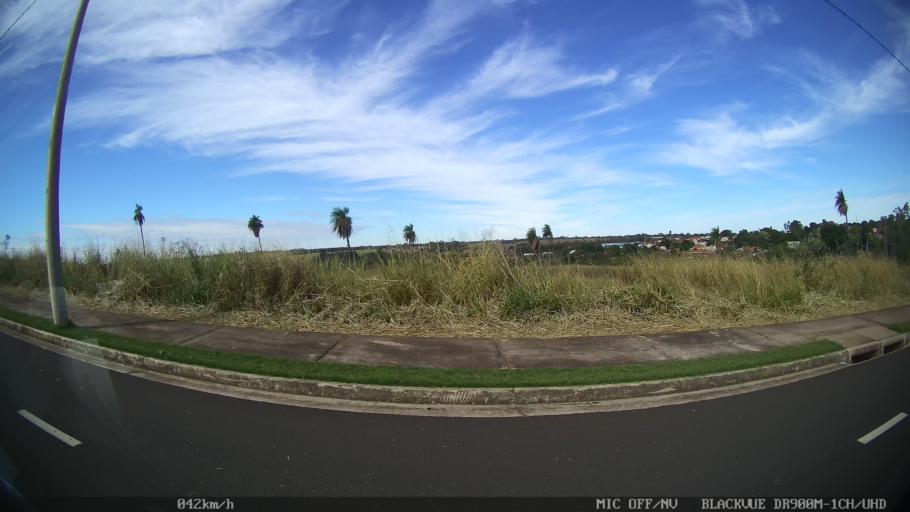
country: BR
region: Sao Paulo
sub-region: Sao Jose Do Rio Preto
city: Sao Jose do Rio Preto
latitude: -20.8583
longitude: -49.3799
